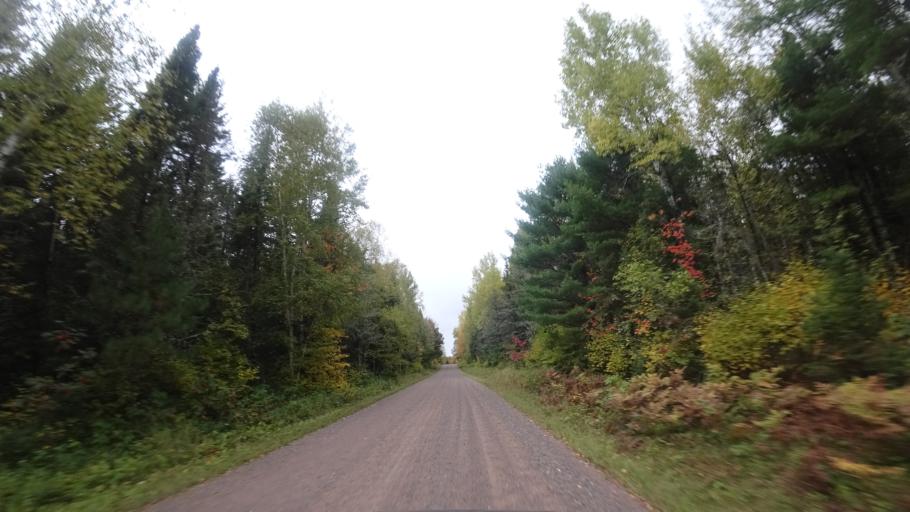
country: US
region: Wisconsin
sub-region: Sawyer County
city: Little Round Lake
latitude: 46.0767
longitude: -90.9924
